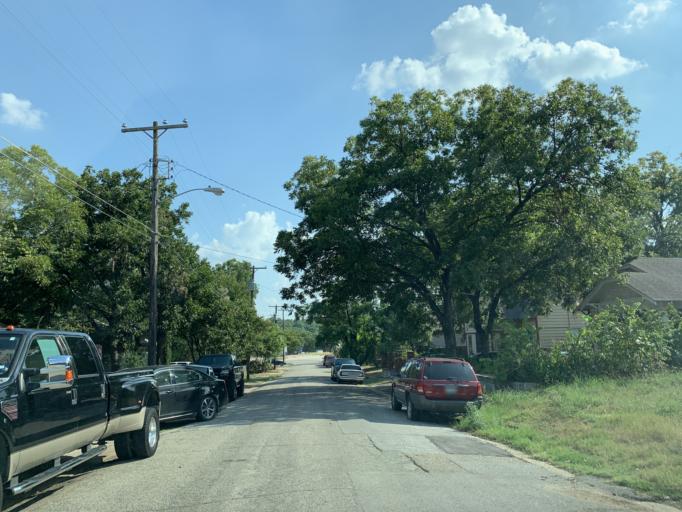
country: US
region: Texas
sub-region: Dallas County
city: Dallas
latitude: 32.7459
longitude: -96.8084
